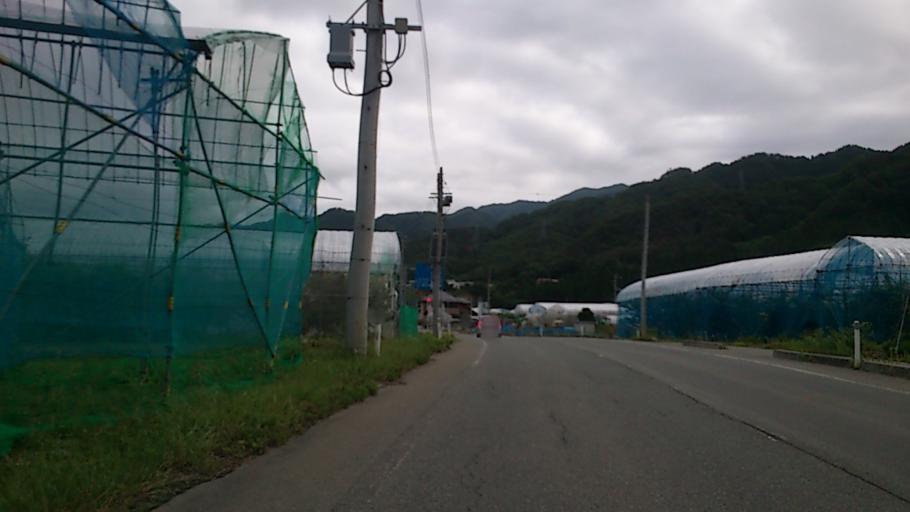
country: JP
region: Yamagata
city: Tendo
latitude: 38.3119
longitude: 140.4090
